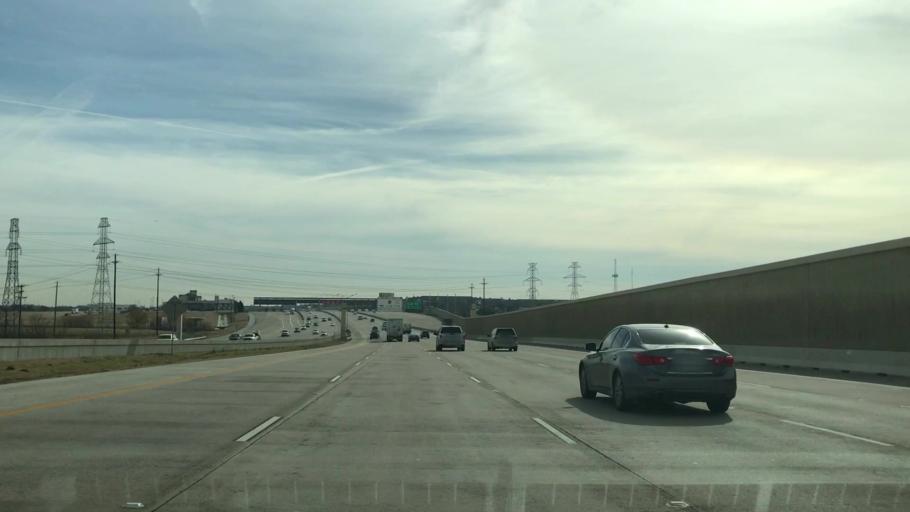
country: US
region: Texas
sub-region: Dallas County
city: Addison
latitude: 33.0065
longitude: -96.7825
